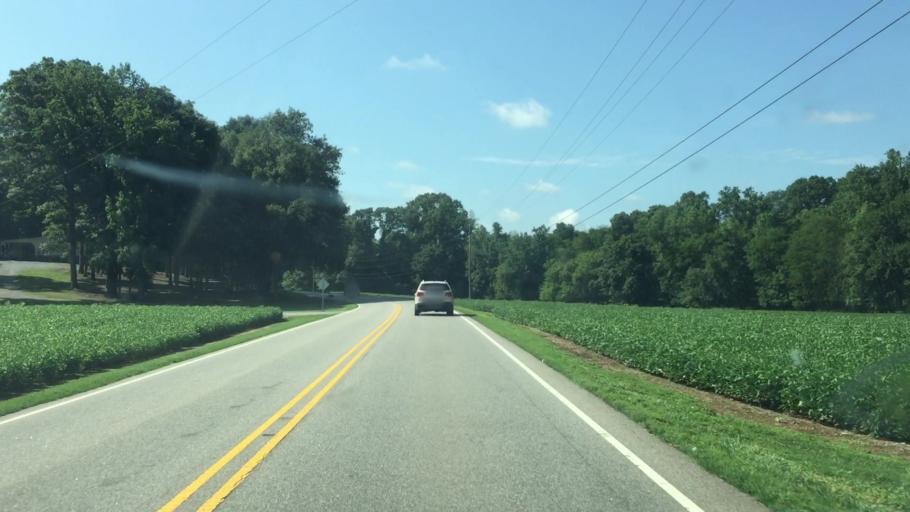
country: US
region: North Carolina
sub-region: Anson County
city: Burnsville
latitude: 35.1125
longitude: -80.3374
